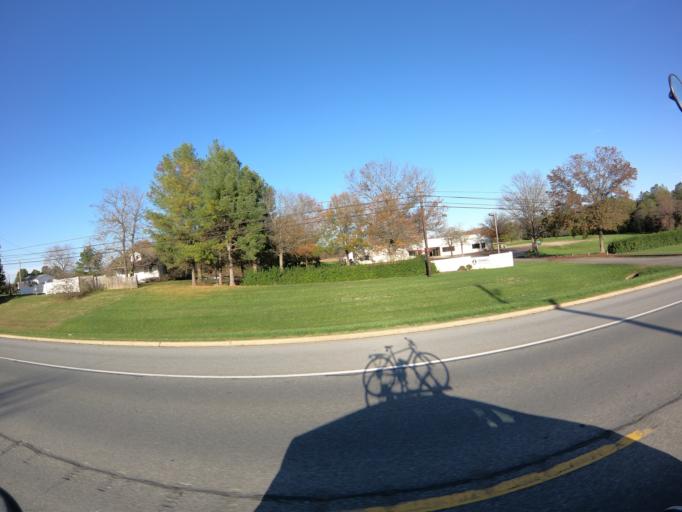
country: US
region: Maryland
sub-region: Saint Mary's County
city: Leonardtown
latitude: 38.3216
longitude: -76.6735
